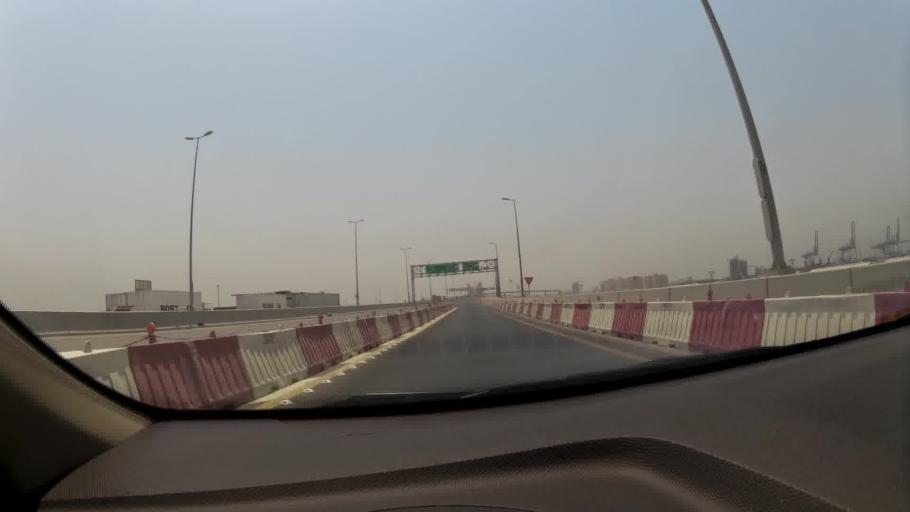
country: KW
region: Al Asimah
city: Ash Shamiyah
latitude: 29.3454
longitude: 47.9334
